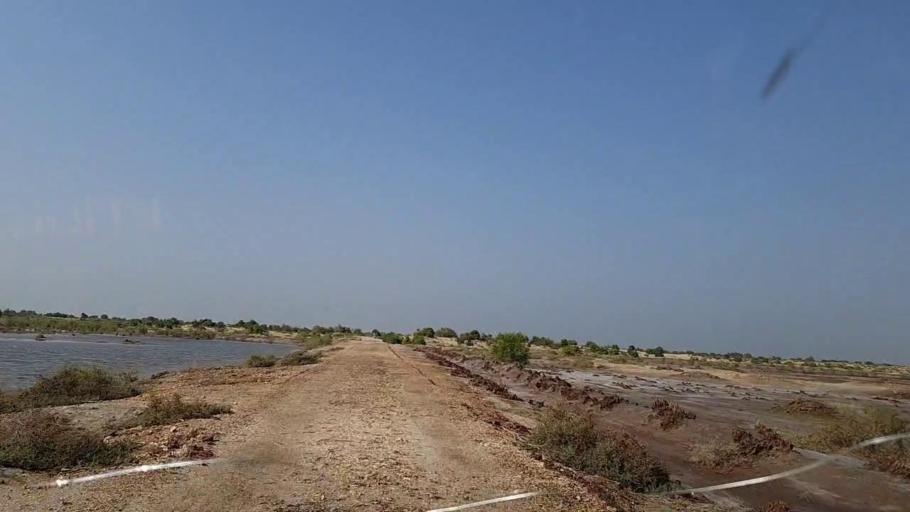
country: PK
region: Sindh
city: Khanpur
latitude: 27.6958
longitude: 69.3844
